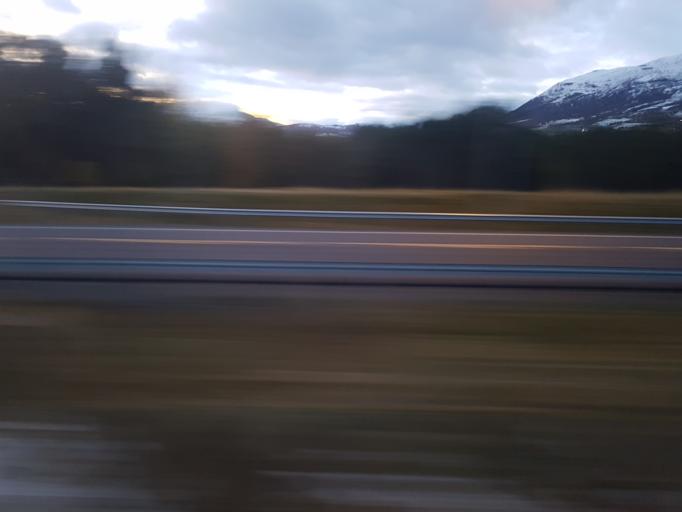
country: NO
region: Sor-Trondelag
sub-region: Oppdal
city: Oppdal
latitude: 62.5854
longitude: 9.6616
